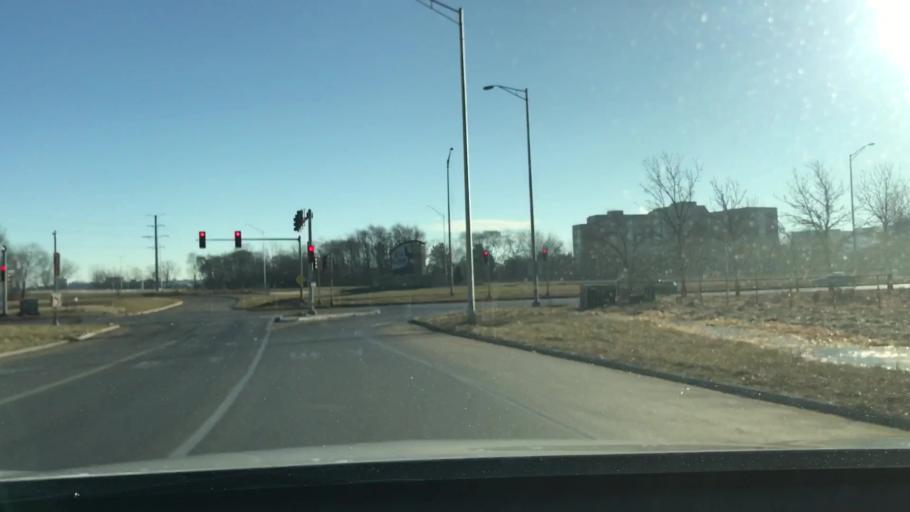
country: US
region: Illinois
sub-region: Cook County
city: Elk Grove Village
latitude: 42.0388
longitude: -87.9850
